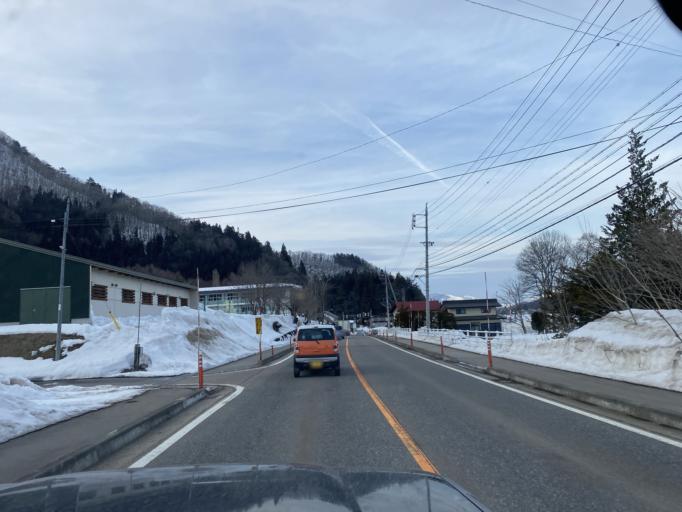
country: JP
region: Nagano
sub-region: Kitaazumi Gun
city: Hakuba
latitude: 36.6448
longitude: 137.8444
